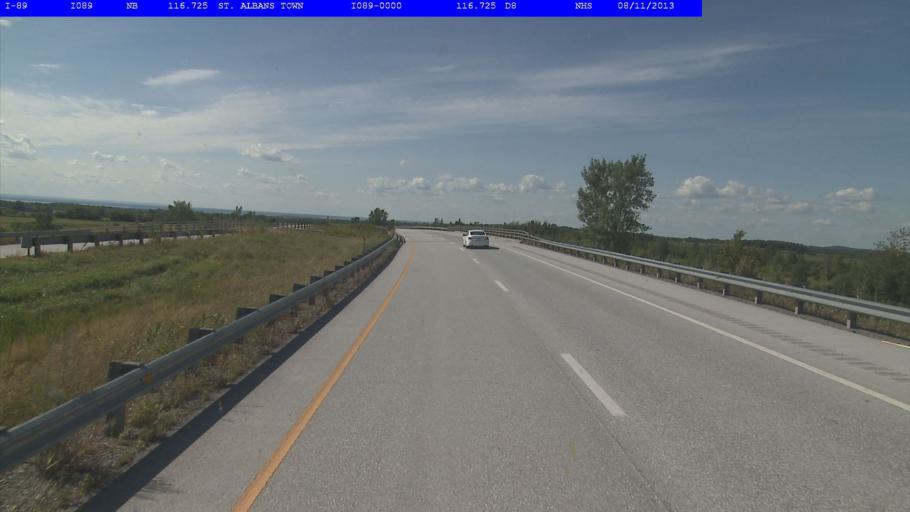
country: US
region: Vermont
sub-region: Franklin County
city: Saint Albans
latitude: 44.8369
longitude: -73.0636
